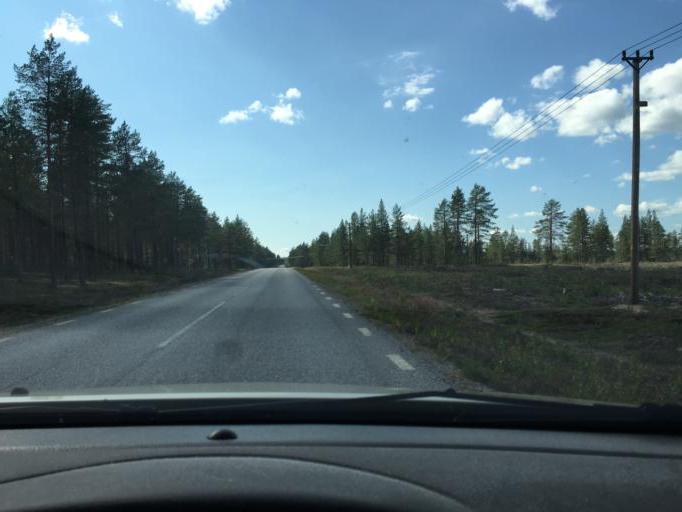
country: SE
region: Norrbotten
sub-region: Kalix Kommun
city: Toere
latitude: 66.0531
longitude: 22.5119
